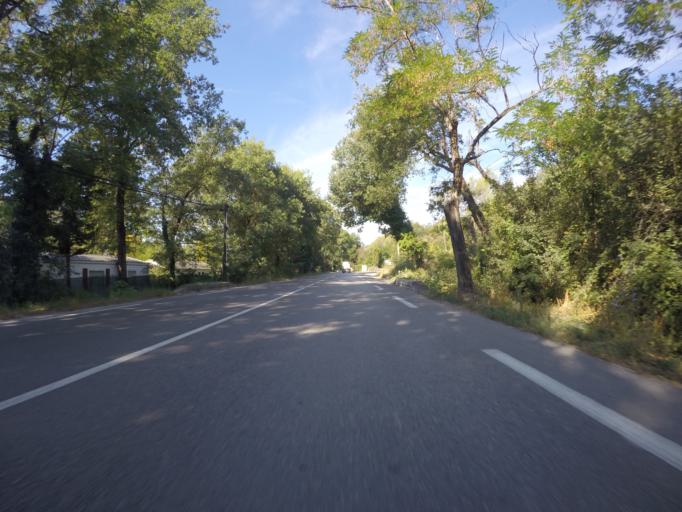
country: FR
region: Provence-Alpes-Cote d'Azur
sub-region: Departement des Alpes-Maritimes
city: Villeneuve-Loubet
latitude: 43.6604
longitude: 7.0995
